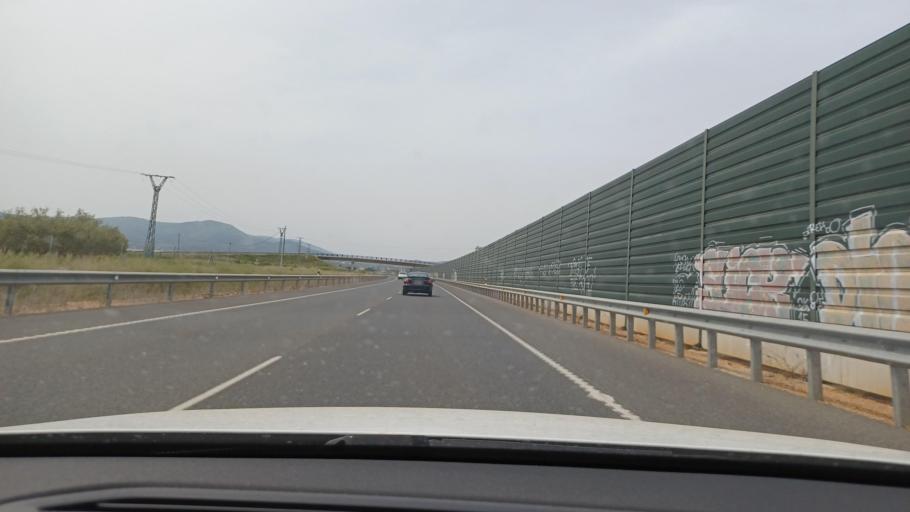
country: ES
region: Valencia
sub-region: Provincia de Castello
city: Benicarlo
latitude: 40.4247
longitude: 0.3952
